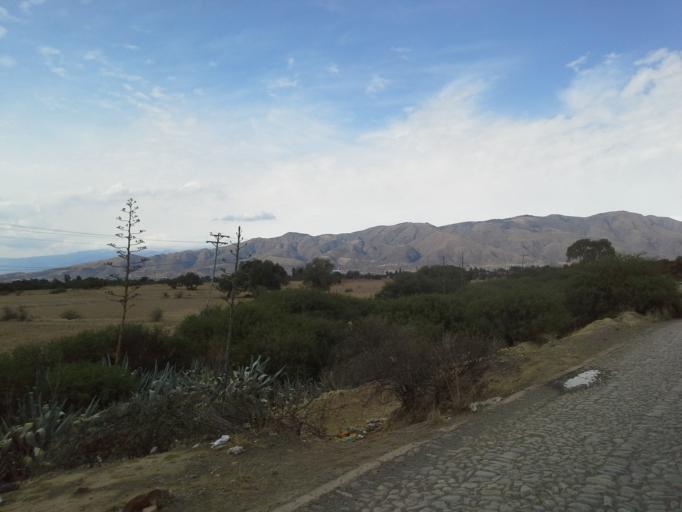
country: BO
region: Cochabamba
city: Tarata
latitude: -17.6037
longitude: -66.0203
